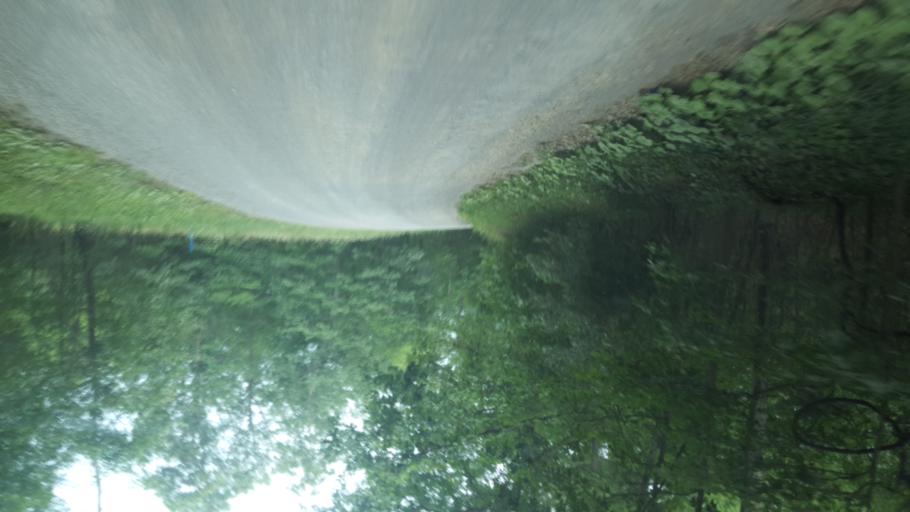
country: US
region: Pennsylvania
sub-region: Clarion County
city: Clarion
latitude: 41.2214
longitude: -79.4103
